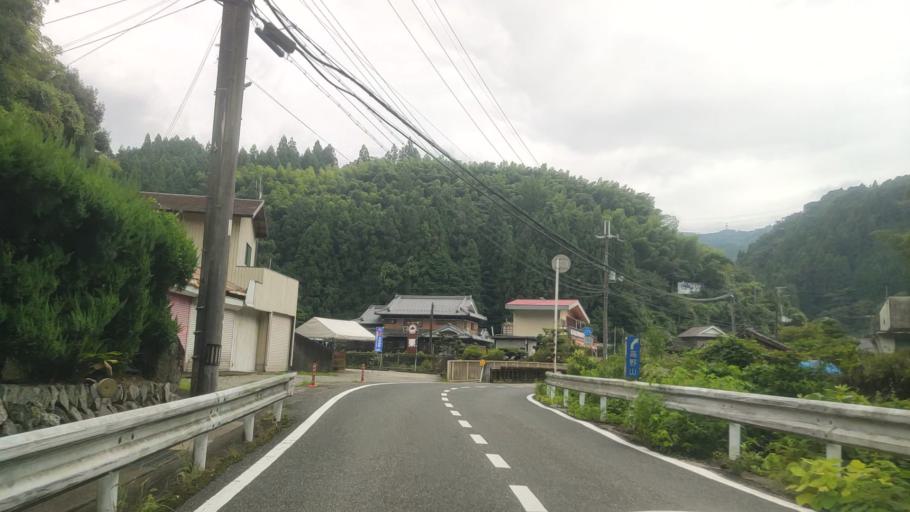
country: JP
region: Wakayama
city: Hashimoto
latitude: 34.2641
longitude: 135.5509
